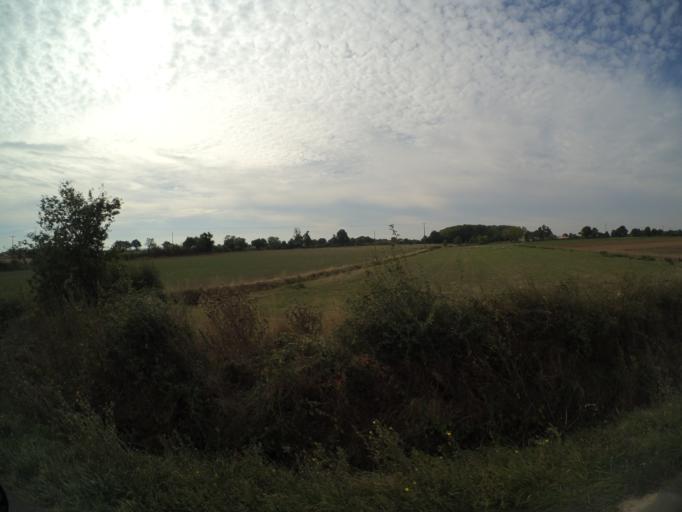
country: FR
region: Pays de la Loire
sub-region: Departement de Maine-et-Loire
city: Melay
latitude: 47.2095
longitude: -0.6845
